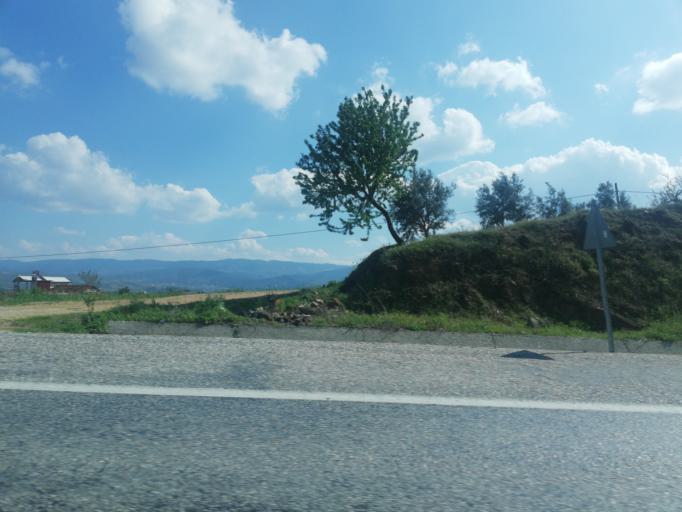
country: TR
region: Manisa
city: Sarigol
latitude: 38.1848
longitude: 28.6748
